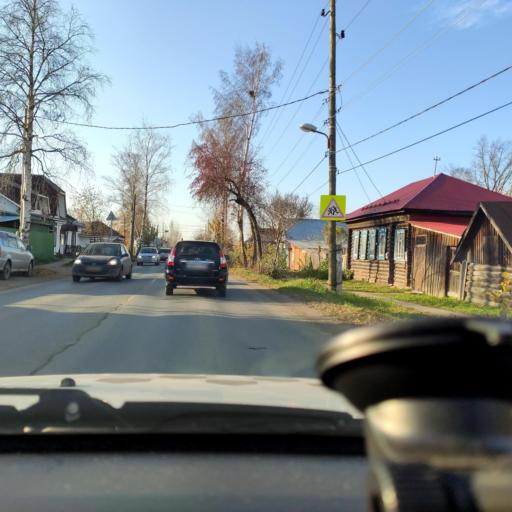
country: RU
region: Perm
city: Perm
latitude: 58.0480
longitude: 56.3320
